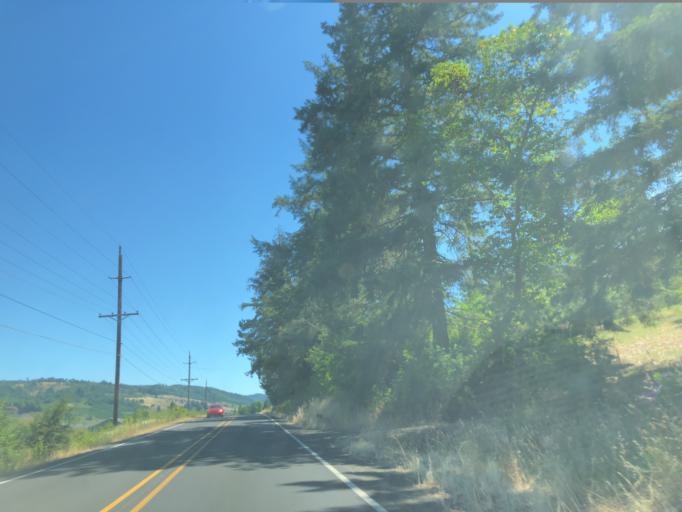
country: US
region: Oregon
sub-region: Douglas County
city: Yoncalla
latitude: 43.5774
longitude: -123.2808
